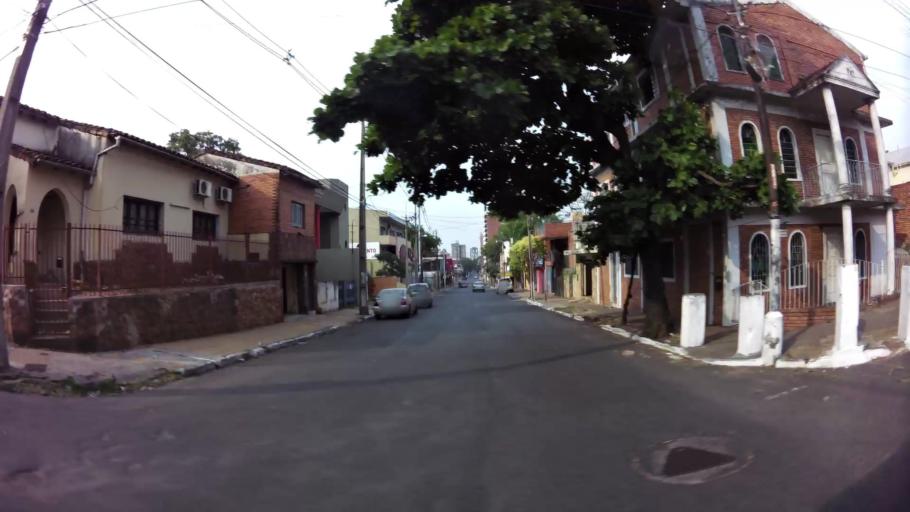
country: PY
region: Asuncion
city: Asuncion
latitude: -25.2971
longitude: -57.6308
